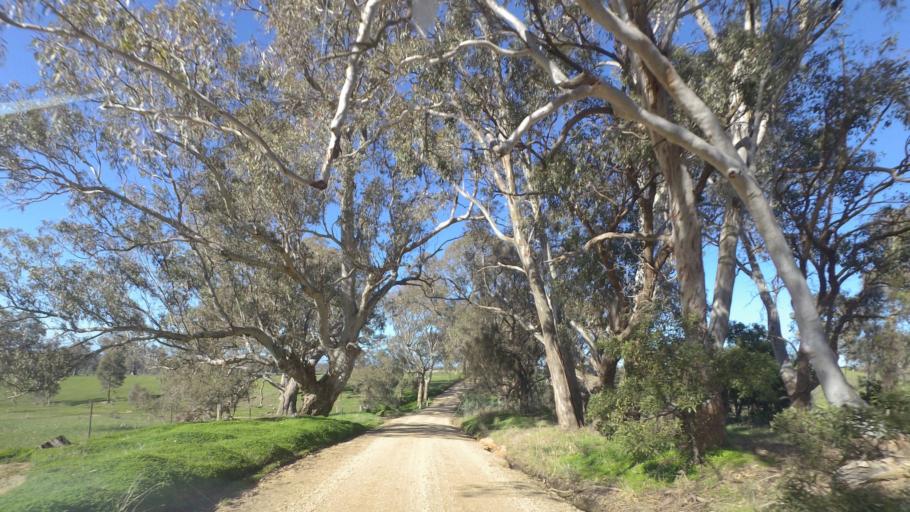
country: AU
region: Victoria
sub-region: Mount Alexander
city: Castlemaine
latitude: -36.9632
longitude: 144.3402
